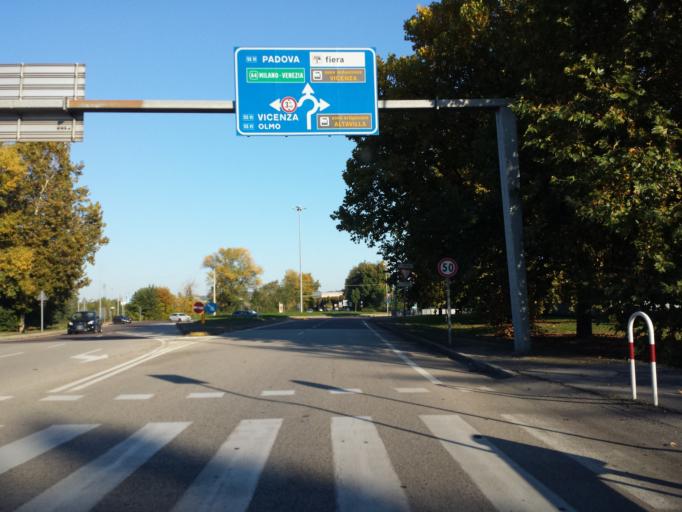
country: IT
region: Veneto
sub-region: Provincia di Vicenza
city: Creazzo
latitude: 45.5217
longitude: 11.4884
